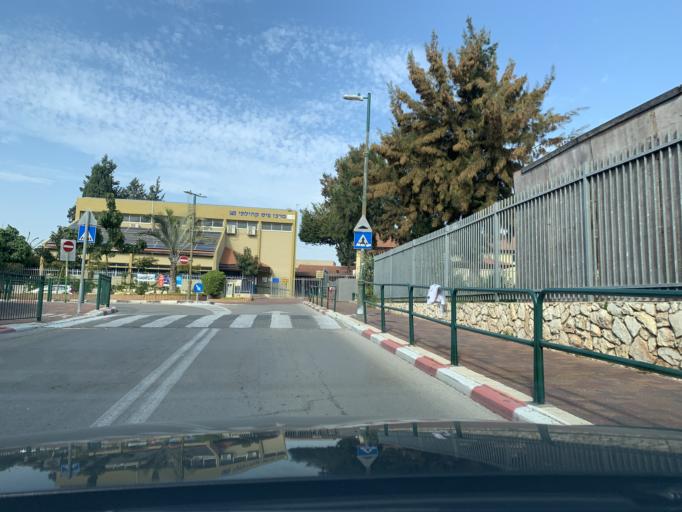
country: IL
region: Tel Aviv
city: Giv`at Shemu'el
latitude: 32.0620
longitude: 34.8549
